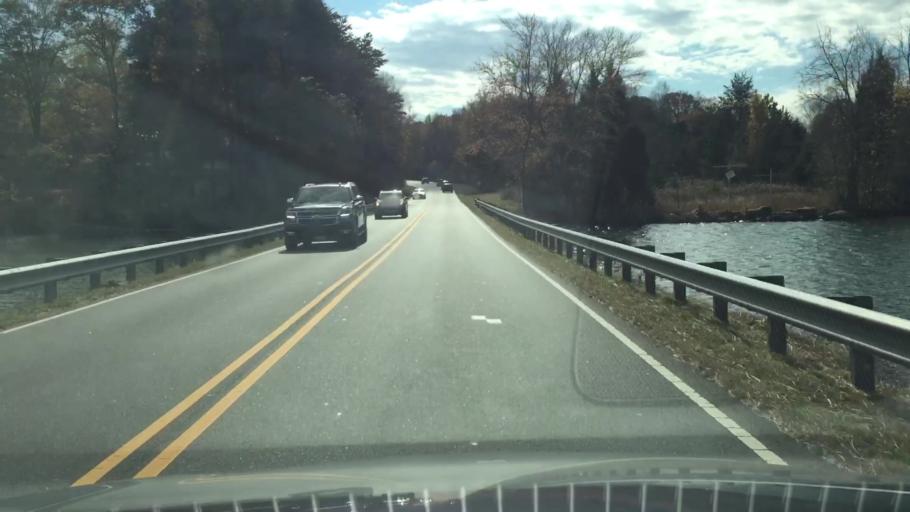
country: US
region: North Carolina
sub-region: Iredell County
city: Mooresville
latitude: 35.5632
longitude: -80.8658
